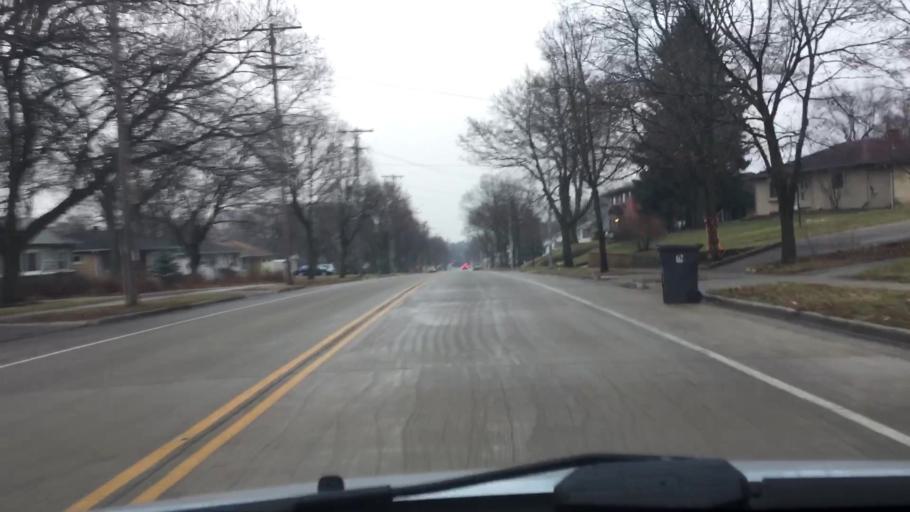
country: US
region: Wisconsin
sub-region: Waukesha County
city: Waukesha
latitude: 43.0205
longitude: -88.2464
